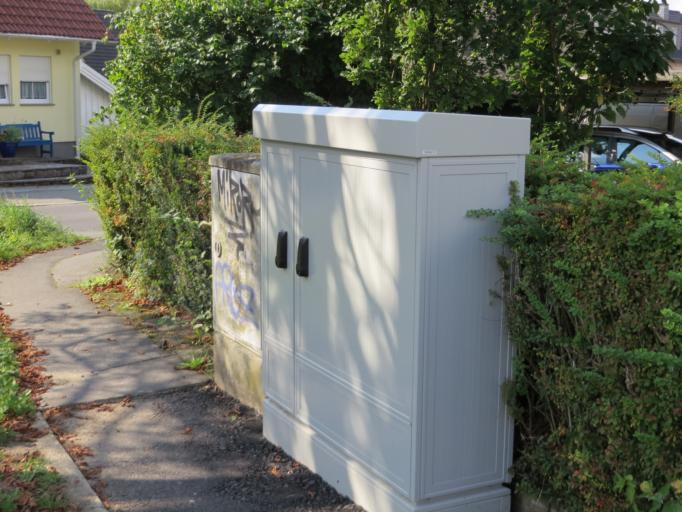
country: DE
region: North Rhine-Westphalia
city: Witten
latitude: 51.4527
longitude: 7.4057
